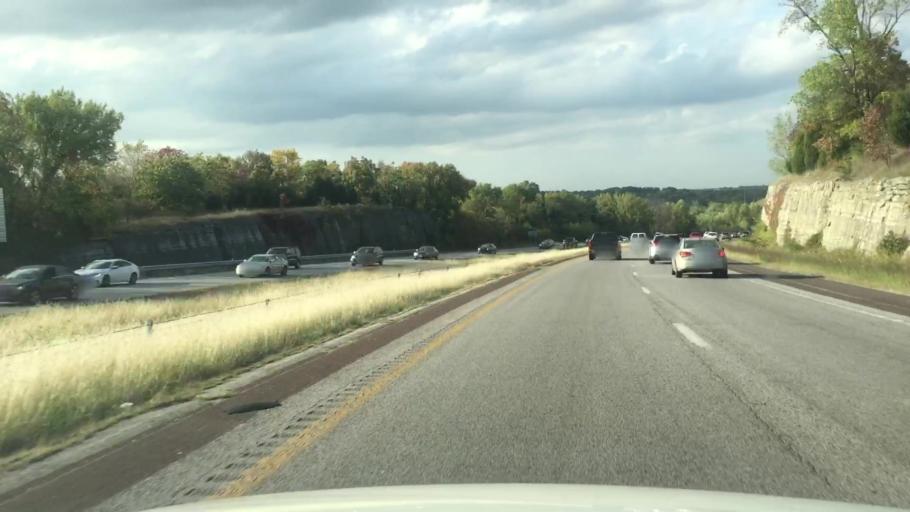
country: US
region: Missouri
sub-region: Jackson County
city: Blue Springs
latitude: 39.0176
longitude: -94.3587
